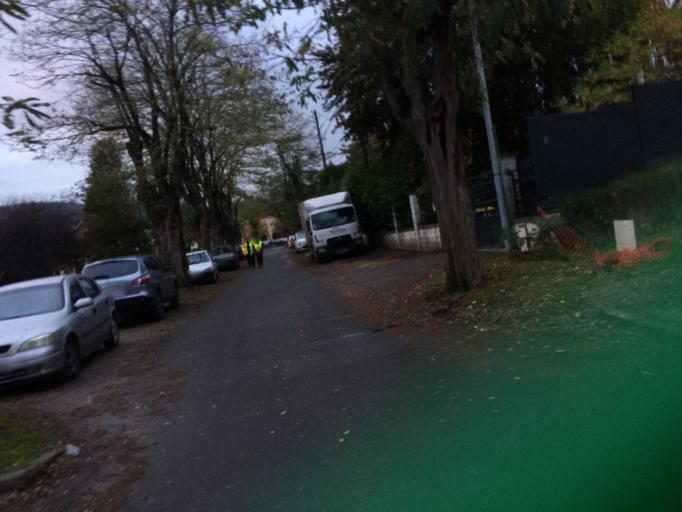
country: FR
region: Ile-de-France
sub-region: Departement de l'Essonne
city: La Ville-du-Bois
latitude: 48.6585
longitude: 2.2685
